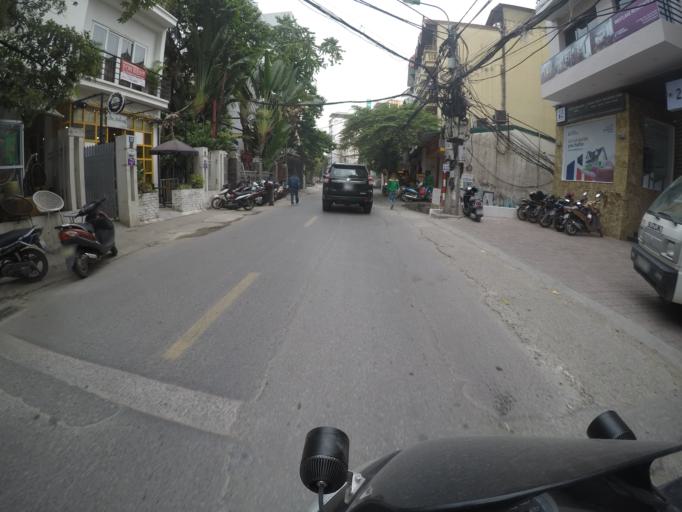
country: VN
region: Ha Noi
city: Tay Ho
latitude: 21.0683
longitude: 105.8247
